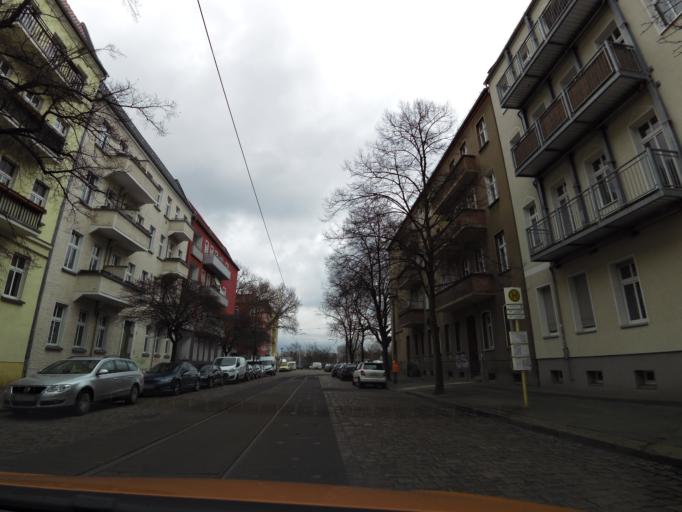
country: DE
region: Berlin
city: Lichtenberg
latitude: 52.5136
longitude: 13.5015
